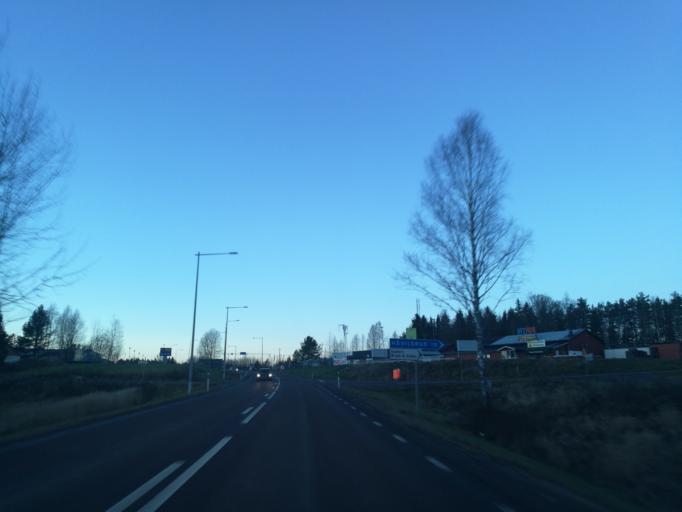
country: SE
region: Vaermland
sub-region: Eda Kommun
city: Charlottenberg
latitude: 59.9194
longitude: 12.2715
